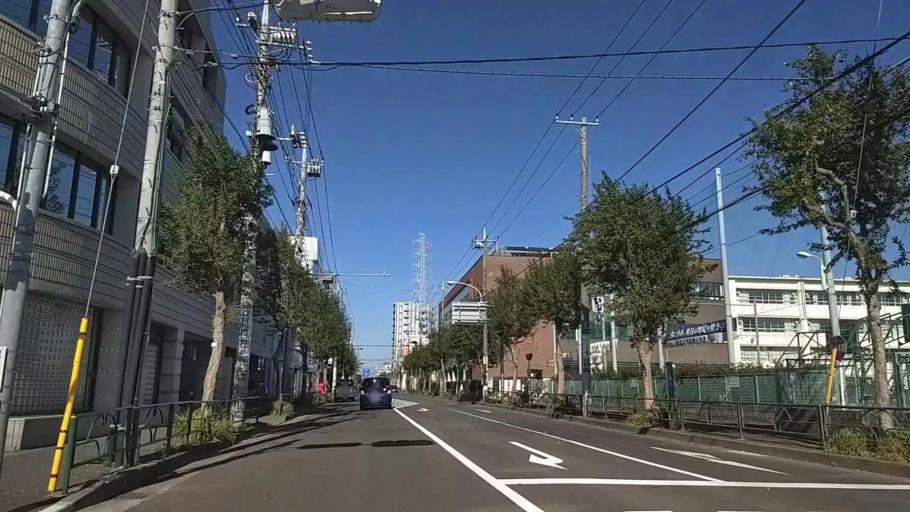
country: JP
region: Tokyo
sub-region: Machida-shi
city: Machida
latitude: 35.5498
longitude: 139.4463
